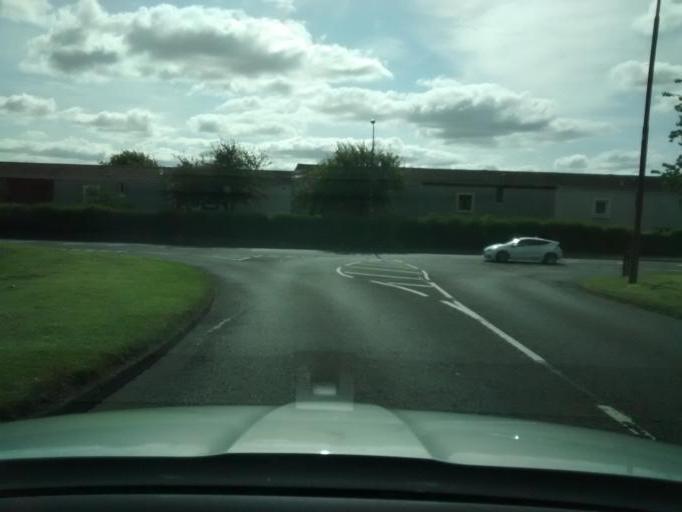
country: GB
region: Scotland
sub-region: West Lothian
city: Mid Calder
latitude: 55.8935
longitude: -3.4961
